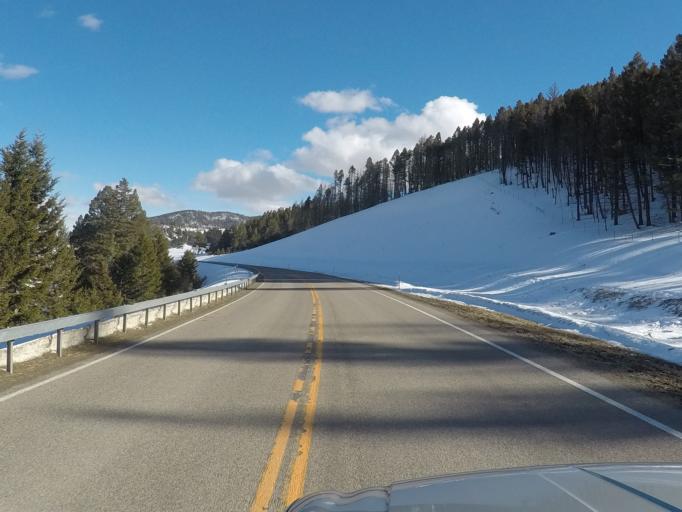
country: US
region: Montana
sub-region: Meagher County
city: White Sulphur Springs
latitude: 46.5515
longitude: -110.4796
